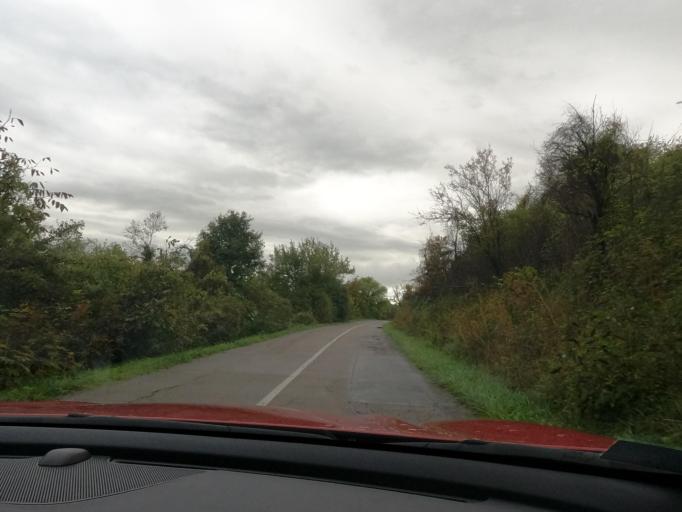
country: HR
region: Sisacko-Moslavacka
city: Glina
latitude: 45.3208
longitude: 16.2169
